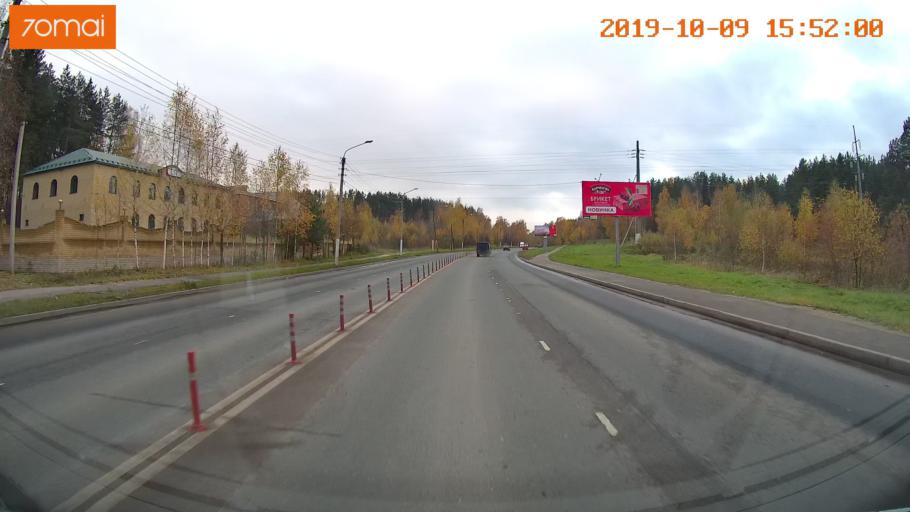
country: RU
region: Kostroma
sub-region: Kostromskoy Rayon
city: Kostroma
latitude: 57.7930
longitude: 40.9734
